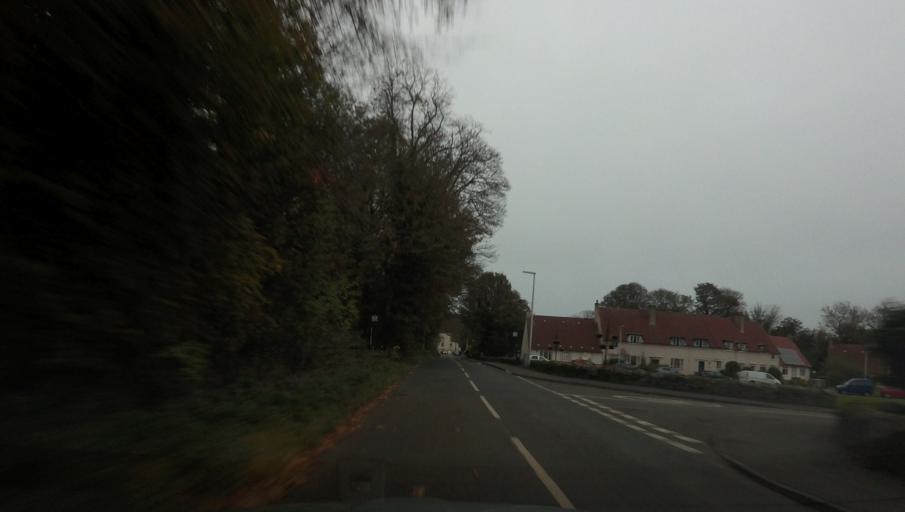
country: GB
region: Scotland
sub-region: Fife
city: Crossford
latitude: 56.0381
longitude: -3.5045
